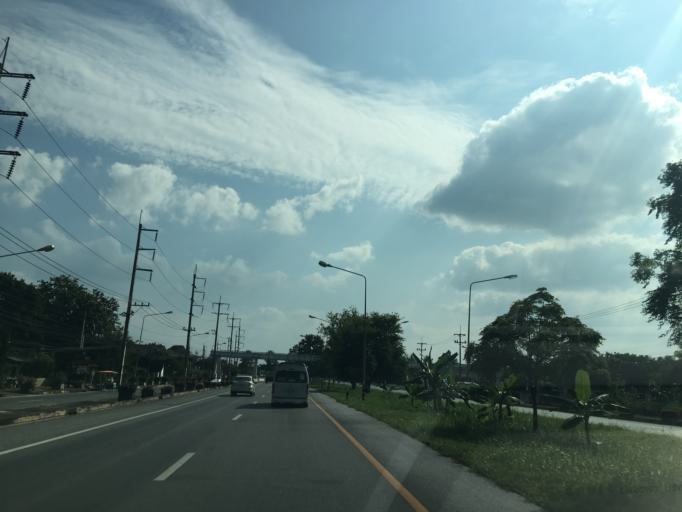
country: TH
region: Chiang Rai
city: Mae Lao
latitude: 19.7216
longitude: 99.7160
